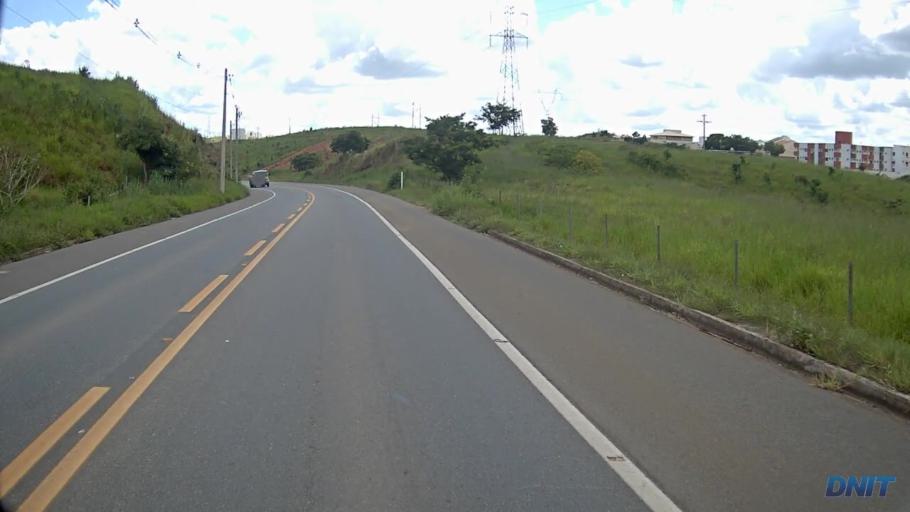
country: BR
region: Minas Gerais
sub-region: Governador Valadares
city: Governador Valadares
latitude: -18.8463
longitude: -41.9809
